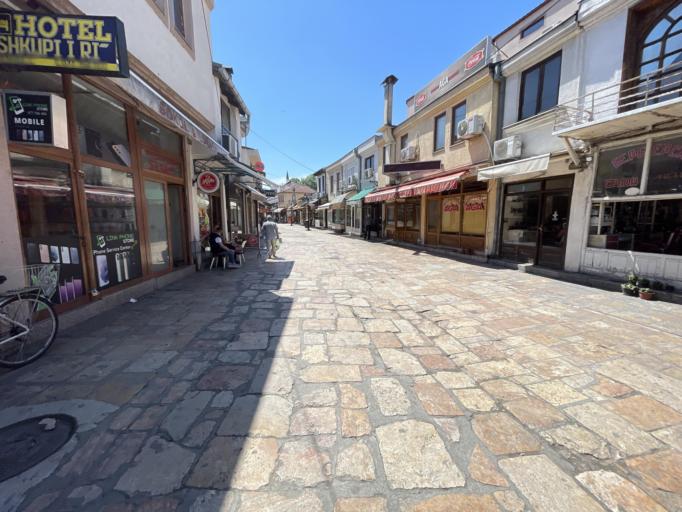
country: MK
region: Karpos
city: Skopje
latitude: 42.0028
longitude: 21.4387
